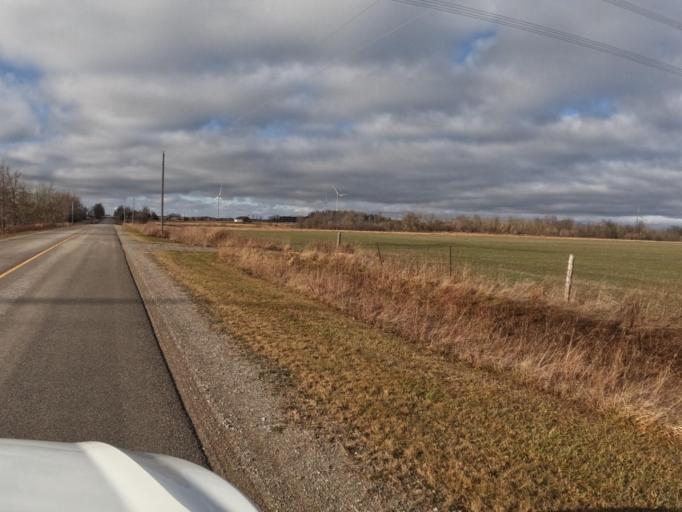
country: CA
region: Ontario
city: Shelburne
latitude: 43.8929
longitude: -80.3447
